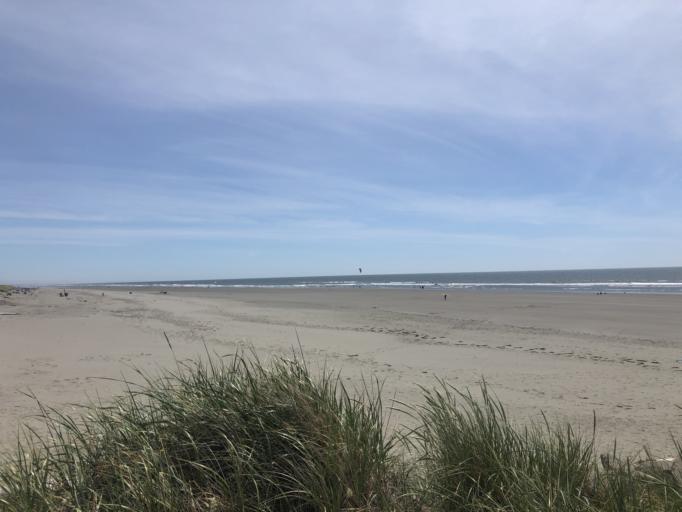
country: US
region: Washington
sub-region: Grays Harbor County
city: Westport
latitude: 46.9050
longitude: -124.1329
